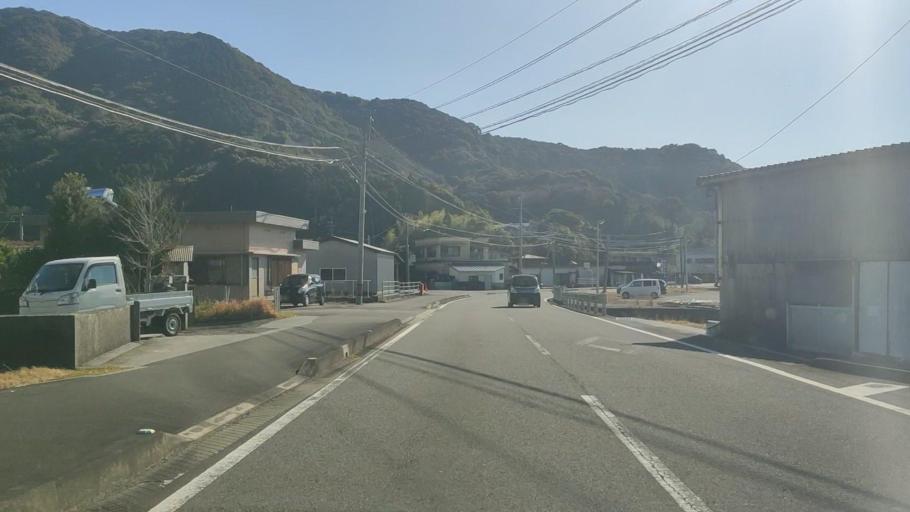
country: JP
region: Oita
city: Saiki
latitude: 32.8028
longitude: 131.8993
